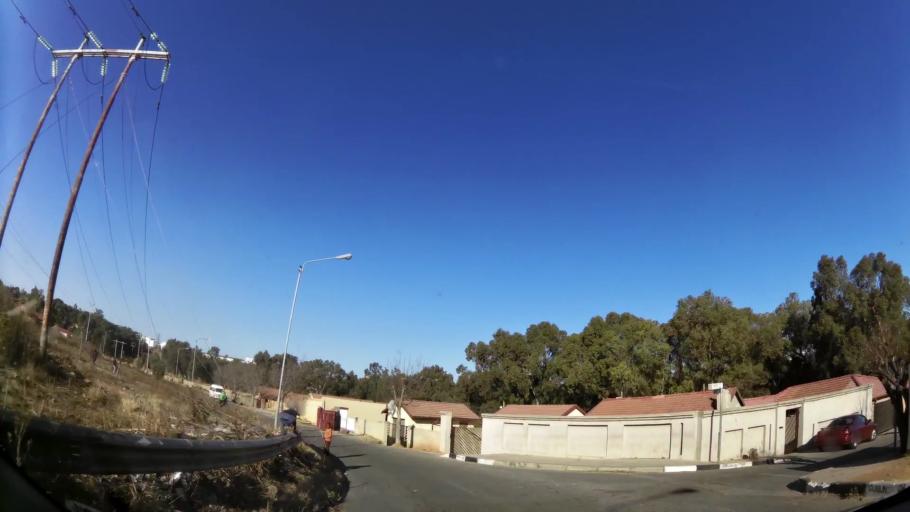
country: ZA
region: Gauteng
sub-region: City of Johannesburg Metropolitan Municipality
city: Johannesburg
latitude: -26.2175
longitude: 27.9868
